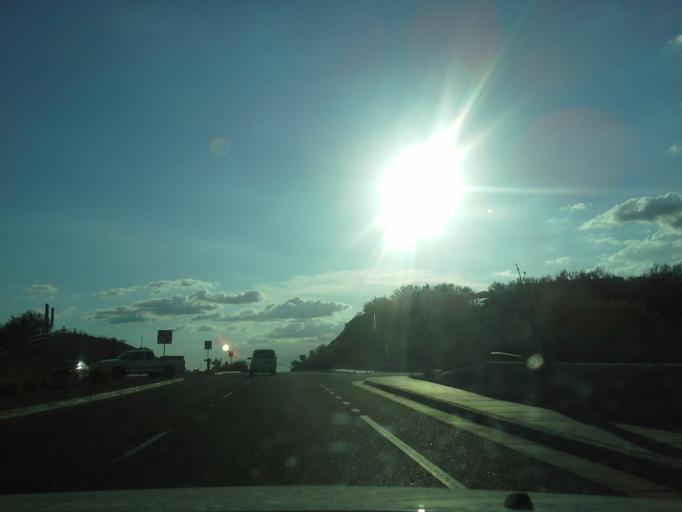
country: US
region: Arizona
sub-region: Pima County
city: Catalina Foothills
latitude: 32.3088
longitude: -110.8760
